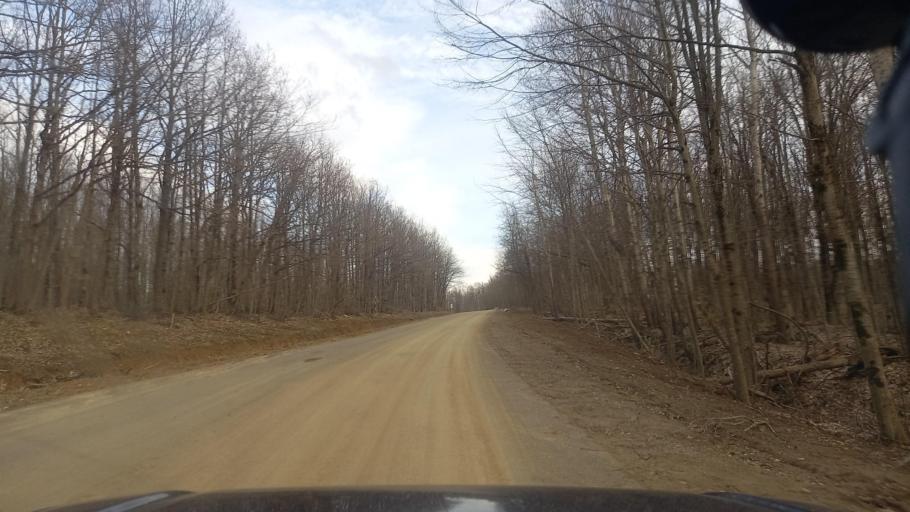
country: RU
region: Krasnodarskiy
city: Goryachiy Klyuch
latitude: 44.7002
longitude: 39.0198
